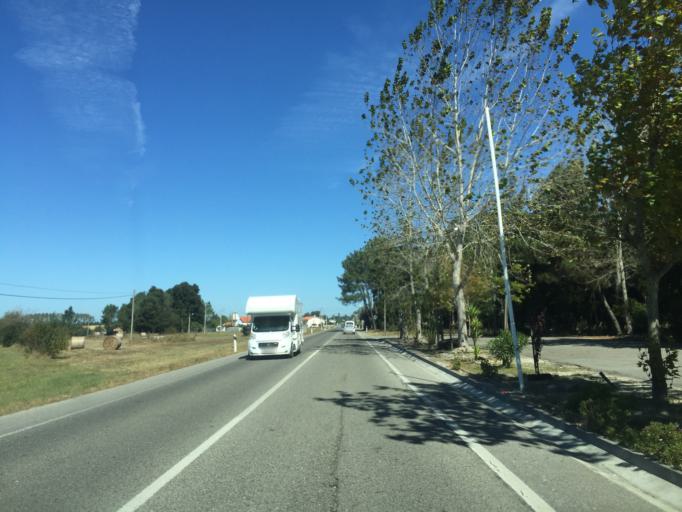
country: PT
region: Coimbra
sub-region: Figueira da Foz
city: Alhadas
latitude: 40.2378
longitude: -8.7945
